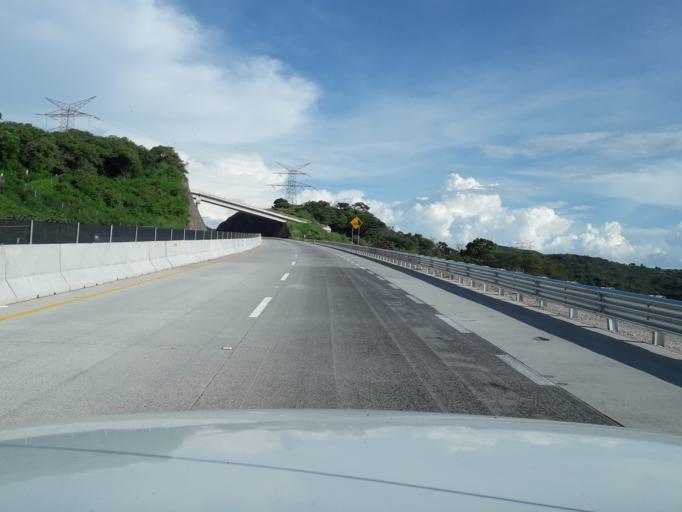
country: MX
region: Jalisco
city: Tala
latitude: 20.5855
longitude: -103.6690
